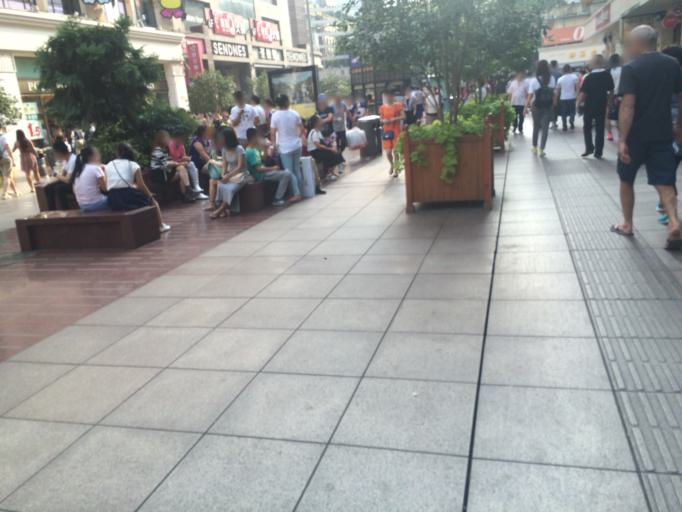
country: CN
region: Shanghai Shi
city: Hongkou
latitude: 31.2387
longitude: 121.4789
